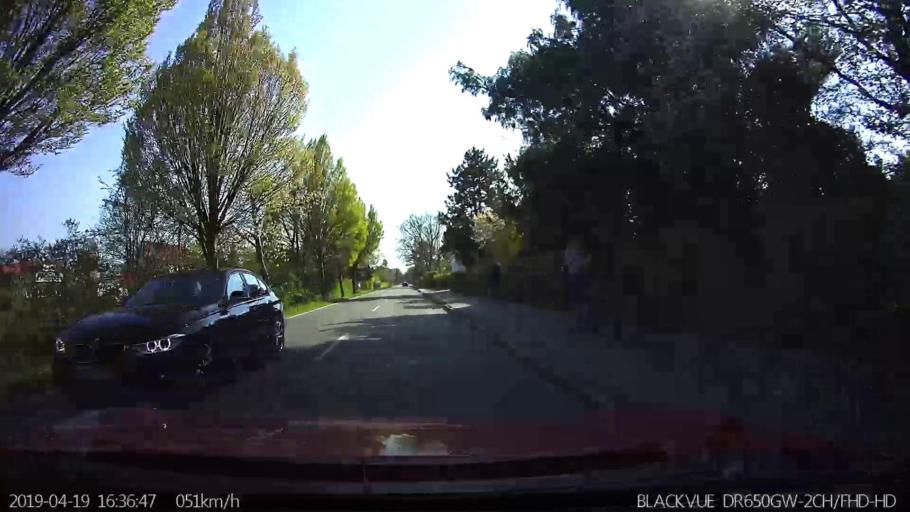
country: DE
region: Schleswig-Holstein
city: Tangstedt
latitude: 53.6618
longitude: 9.8362
